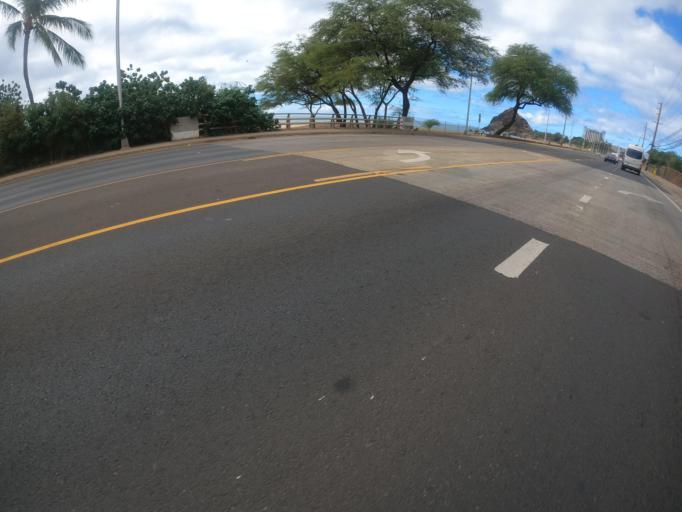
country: US
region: Hawaii
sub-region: Honolulu County
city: Makaha
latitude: 21.4596
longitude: -158.2052
